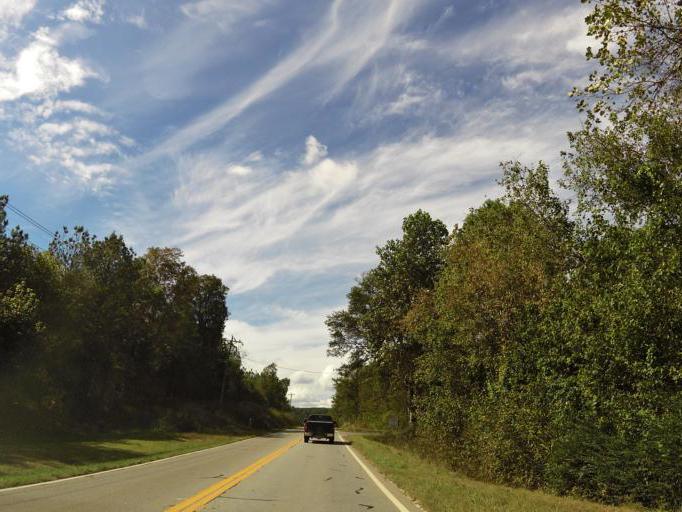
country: US
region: Georgia
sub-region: Pickens County
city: Nelson
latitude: 34.4233
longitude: -84.3278
